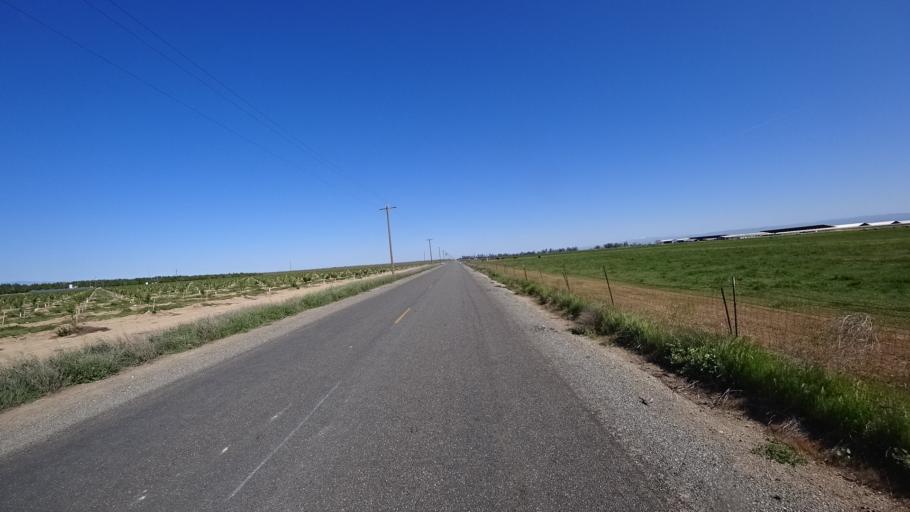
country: US
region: California
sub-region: Glenn County
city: Hamilton City
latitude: 39.6683
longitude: -122.1034
